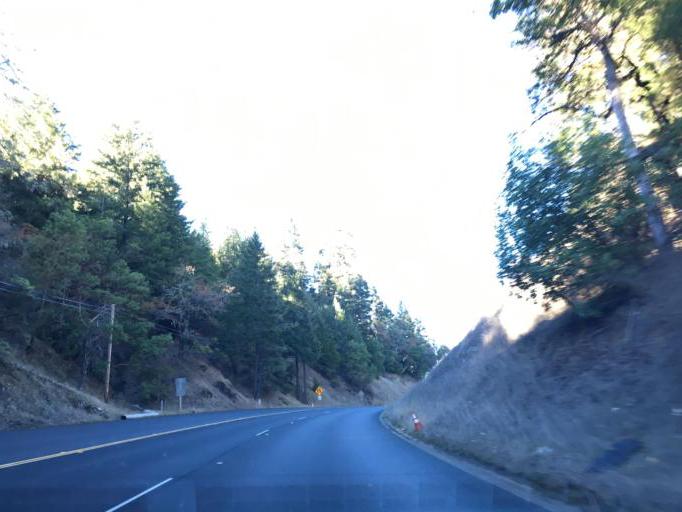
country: US
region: California
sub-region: Mendocino County
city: Laytonville
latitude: 39.7853
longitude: -123.5444
